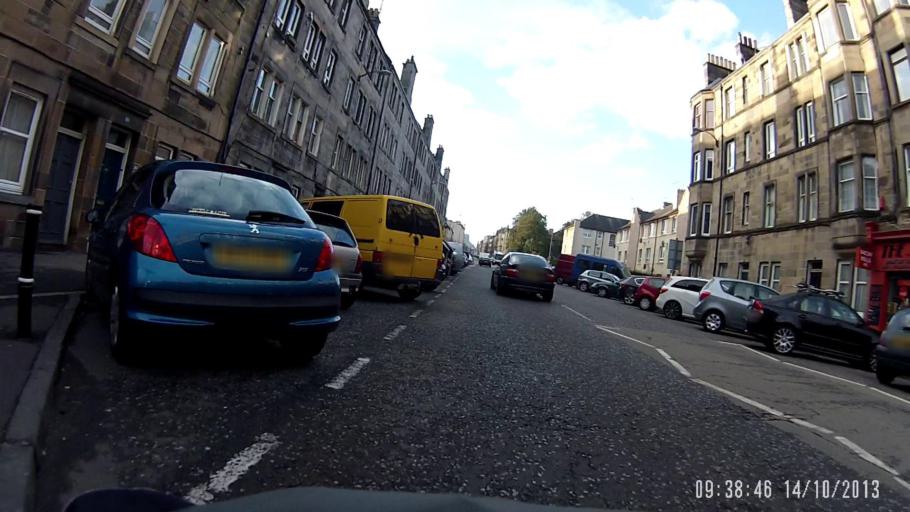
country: GB
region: Scotland
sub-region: West Lothian
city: Seafield
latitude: 55.9653
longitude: -3.1702
